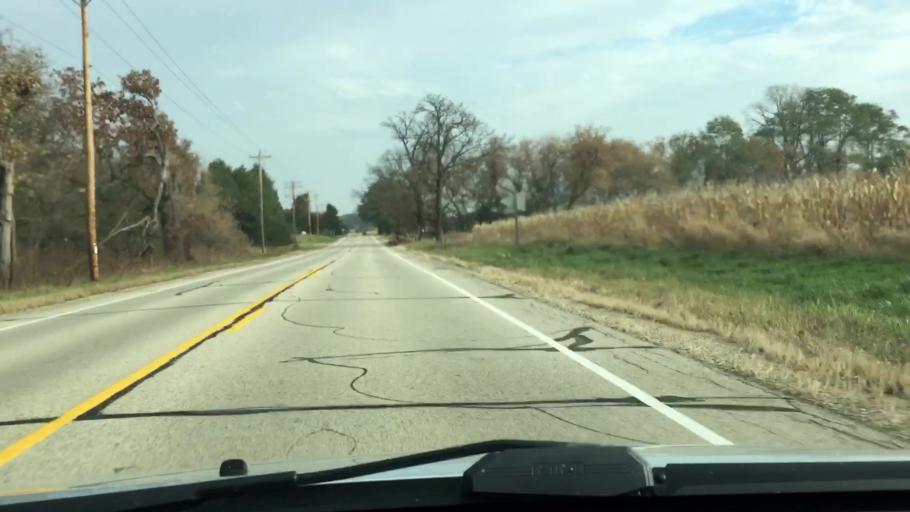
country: US
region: Wisconsin
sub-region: Waukesha County
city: Dousman
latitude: 42.9733
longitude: -88.4711
